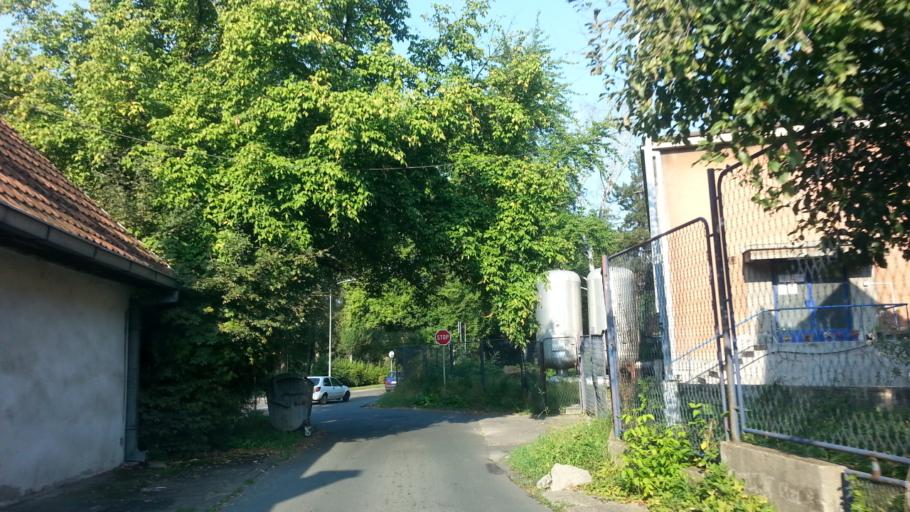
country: RS
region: Central Serbia
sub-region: Belgrade
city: Savski Venac
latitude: 44.7827
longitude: 20.4406
